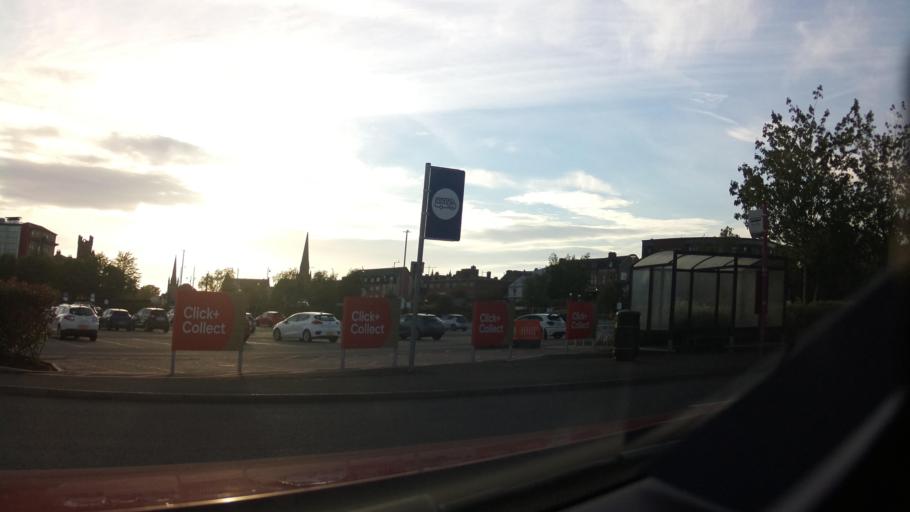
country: GB
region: Scotland
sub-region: Clackmannanshire
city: Alloa
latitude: 56.1142
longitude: -3.7877
